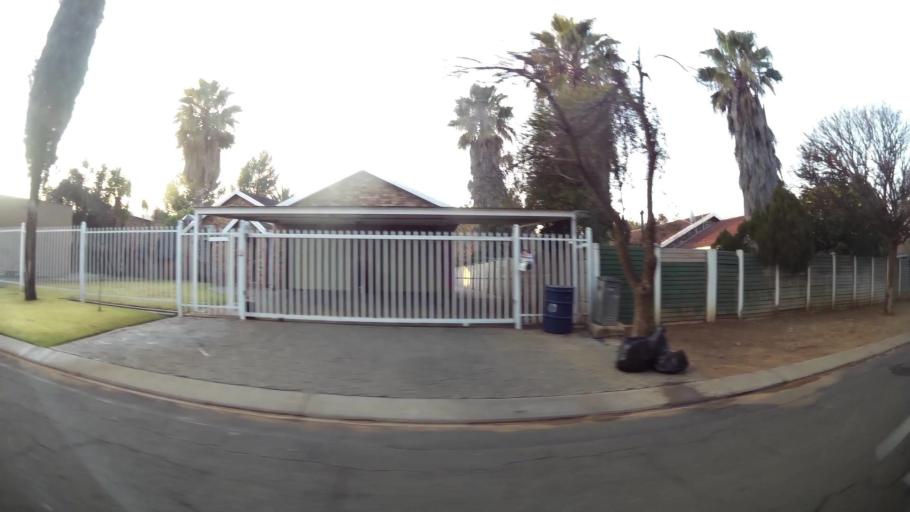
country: ZA
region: Orange Free State
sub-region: Mangaung Metropolitan Municipality
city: Bloemfontein
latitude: -29.1043
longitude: 26.1548
